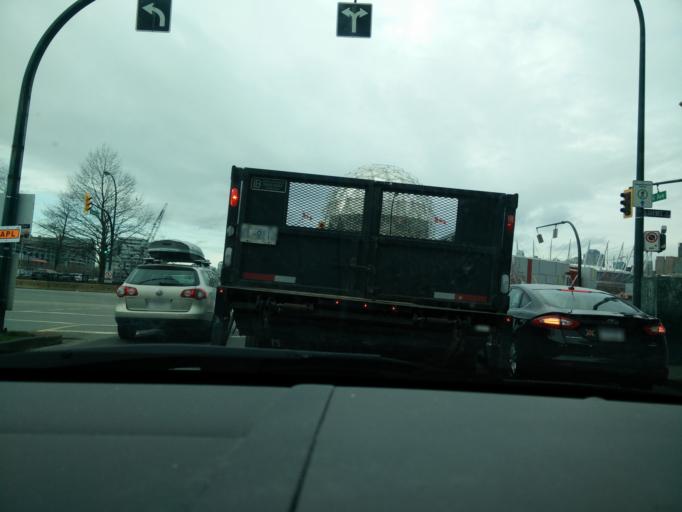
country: CA
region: British Columbia
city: Vancouver
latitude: 49.2732
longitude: -123.1013
